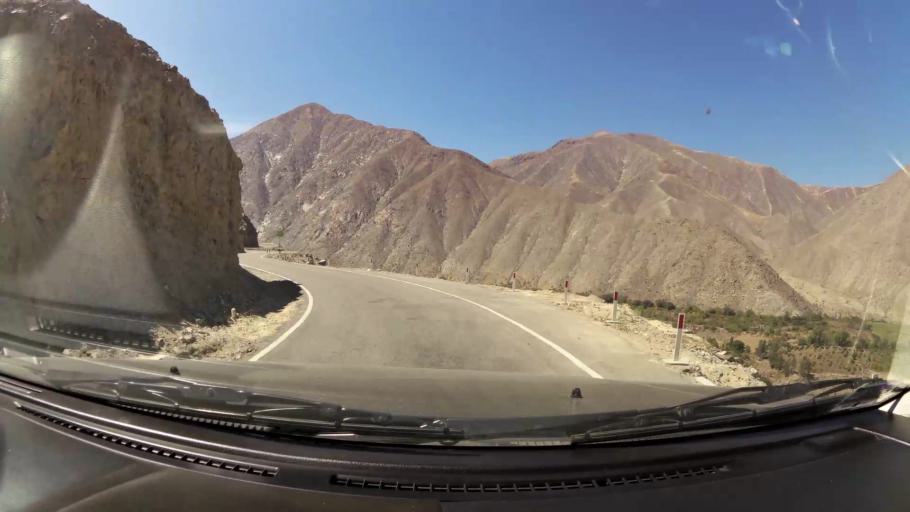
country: PE
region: Ica
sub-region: Provincia de Pisco
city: Huancano
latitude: -13.8336
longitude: -75.5466
